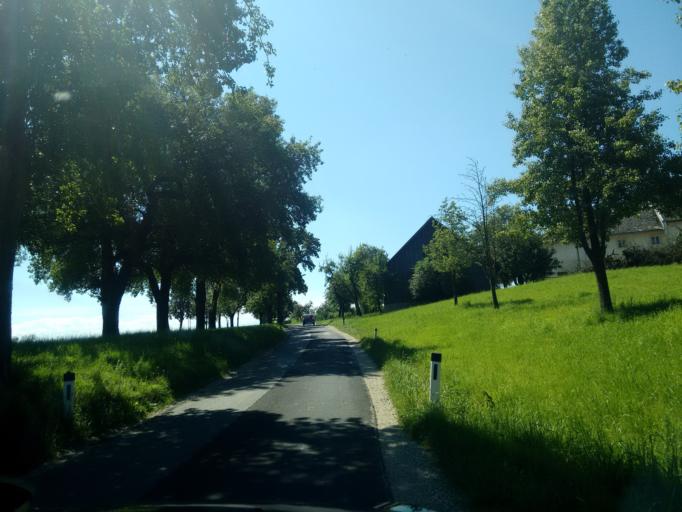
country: AT
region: Upper Austria
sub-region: Wels-Land
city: Gunskirchen
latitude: 48.1787
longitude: 13.9696
